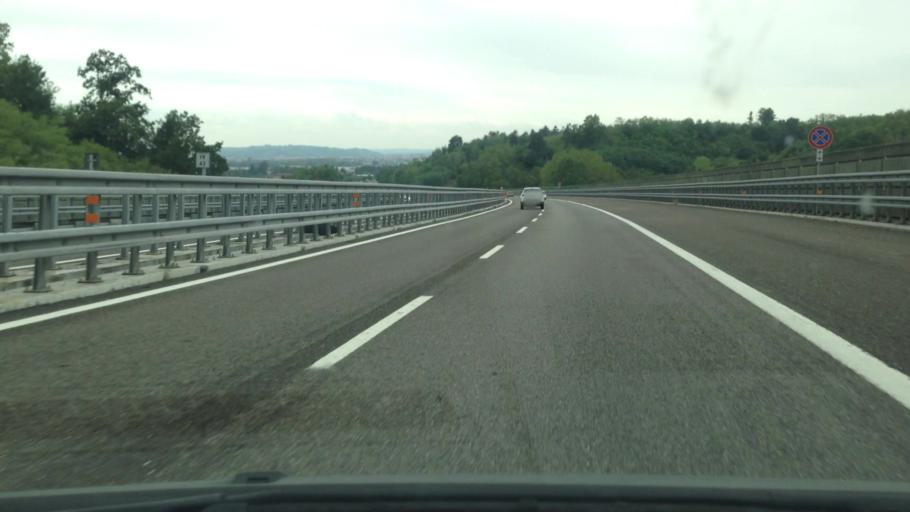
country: IT
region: Piedmont
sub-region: Provincia di Asti
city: Castello di Annone
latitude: 44.9109
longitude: 8.2936
